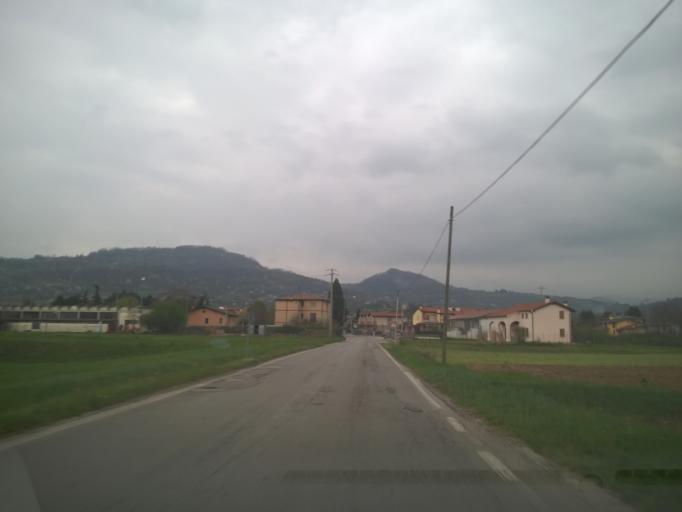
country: IT
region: Veneto
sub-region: Provincia di Vicenza
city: Castelnovo
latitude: 45.6150
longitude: 11.4697
